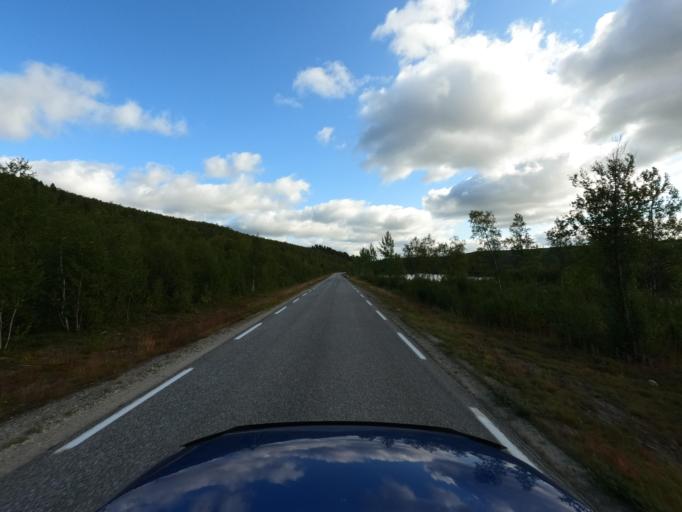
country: NO
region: Finnmark Fylke
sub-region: Porsanger
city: Lakselv
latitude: 69.4237
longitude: 24.8337
